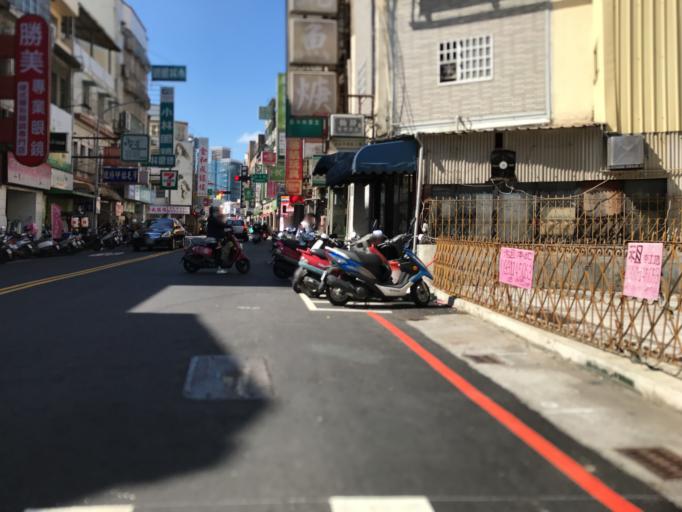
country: TW
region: Taiwan
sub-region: Hsinchu
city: Hsinchu
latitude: 24.8043
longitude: 120.9676
